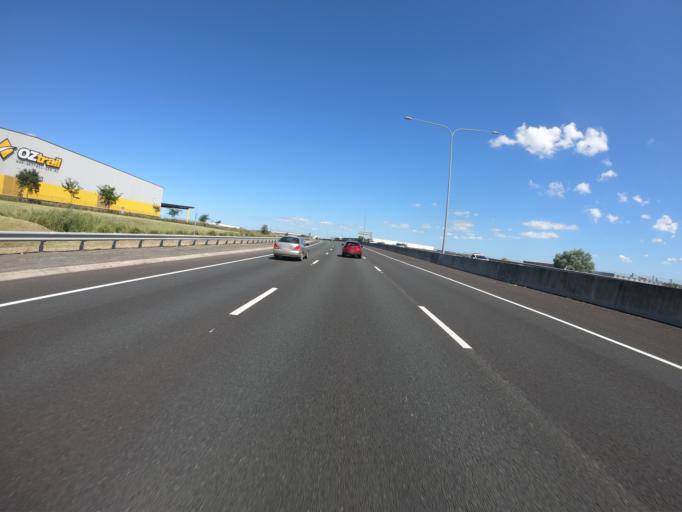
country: AU
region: Queensland
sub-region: Moreton Bay
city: Burpengary
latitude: -27.1521
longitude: 152.9820
